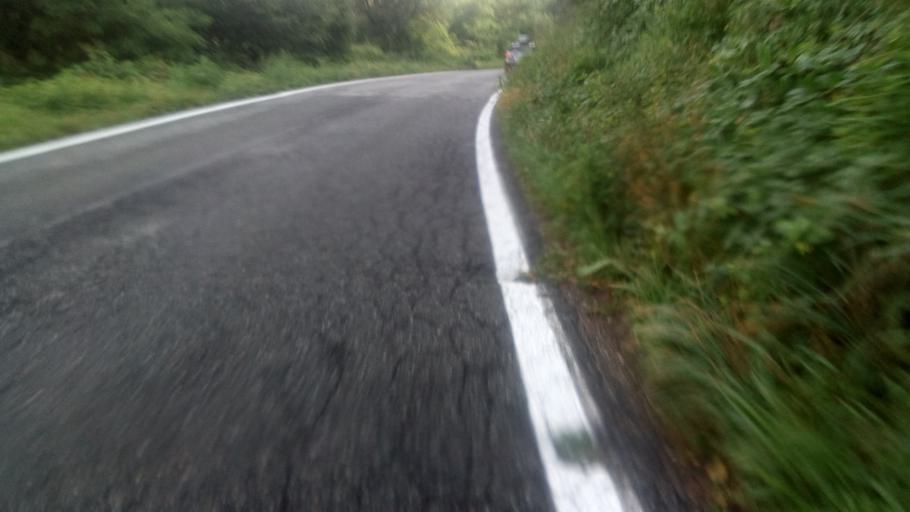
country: IT
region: Piedmont
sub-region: Provincia di Torino
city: Vidracco
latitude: 45.4269
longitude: 7.7608
